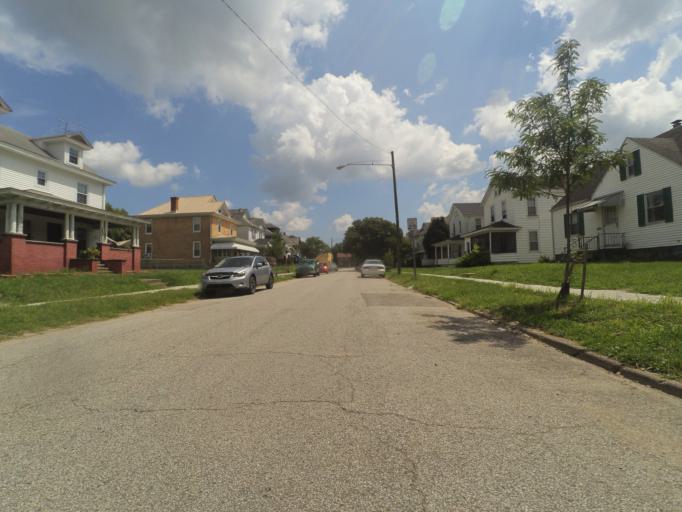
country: US
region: West Virginia
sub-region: Cabell County
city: Huntington
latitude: 38.4162
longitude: -82.4222
